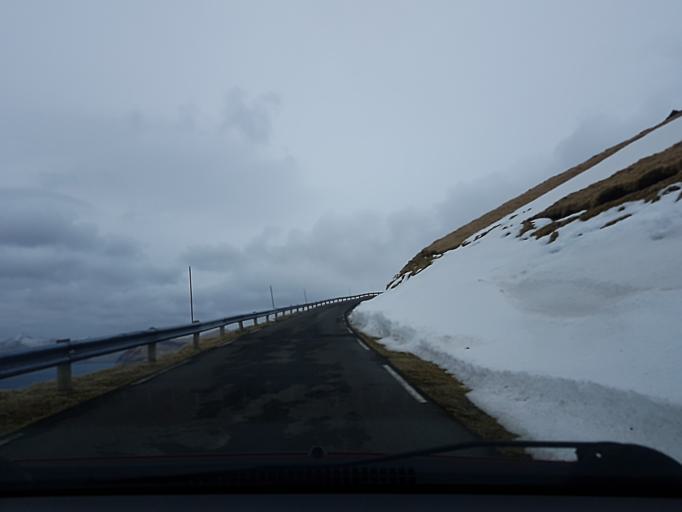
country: FO
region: Streymoy
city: Kollafjordhur
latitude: 62.0047
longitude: -6.9078
